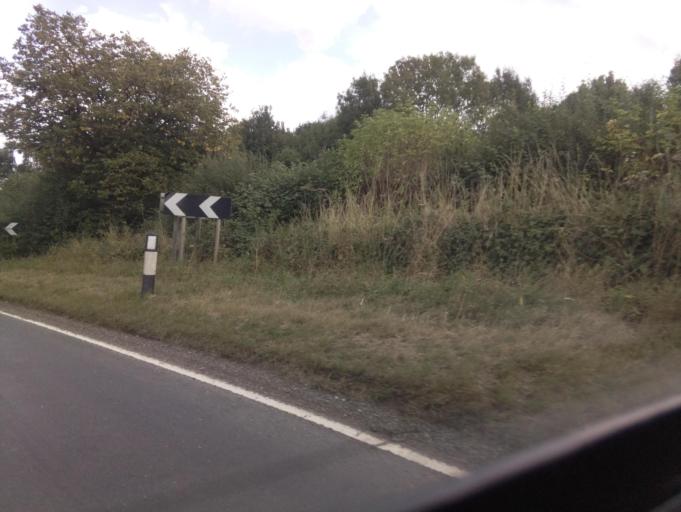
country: GB
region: England
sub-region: North Yorkshire
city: Harrogate
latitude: 54.0513
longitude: -1.5408
